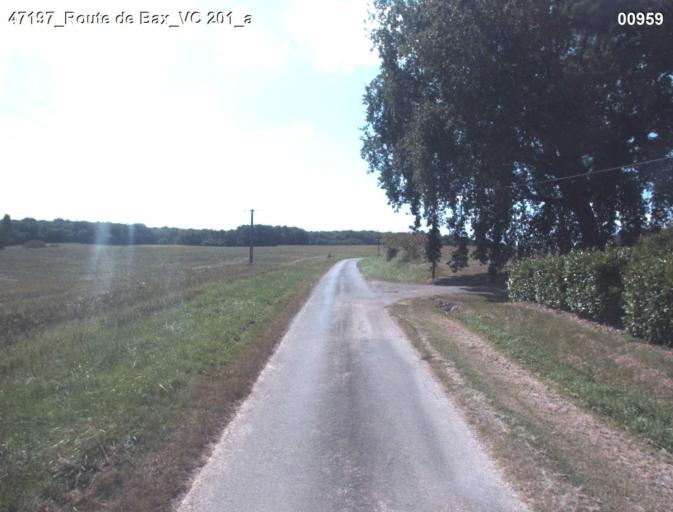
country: FR
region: Aquitaine
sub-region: Departement du Lot-et-Garonne
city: Laplume
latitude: 44.0712
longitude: 0.4856
